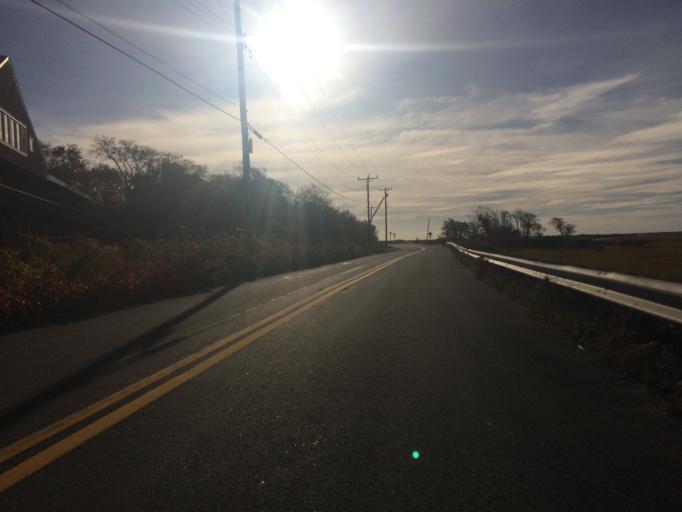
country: US
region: Massachusetts
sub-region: Barnstable County
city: Provincetown
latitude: 42.0385
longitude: -70.1990
